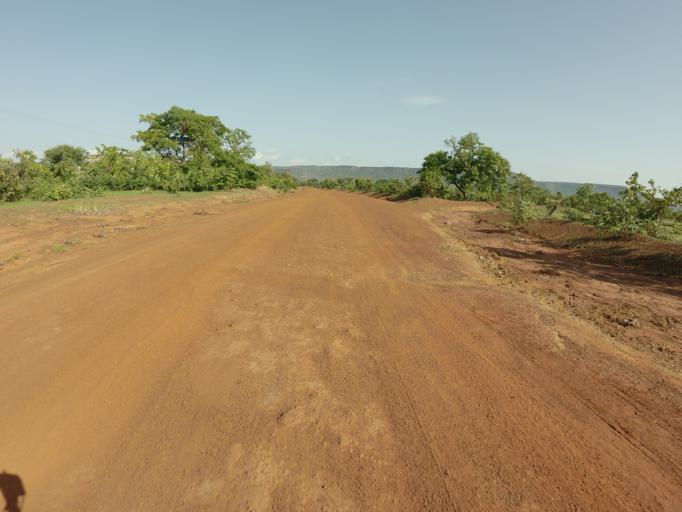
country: GH
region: Upper East
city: Bawku
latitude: 10.6847
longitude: -0.2152
